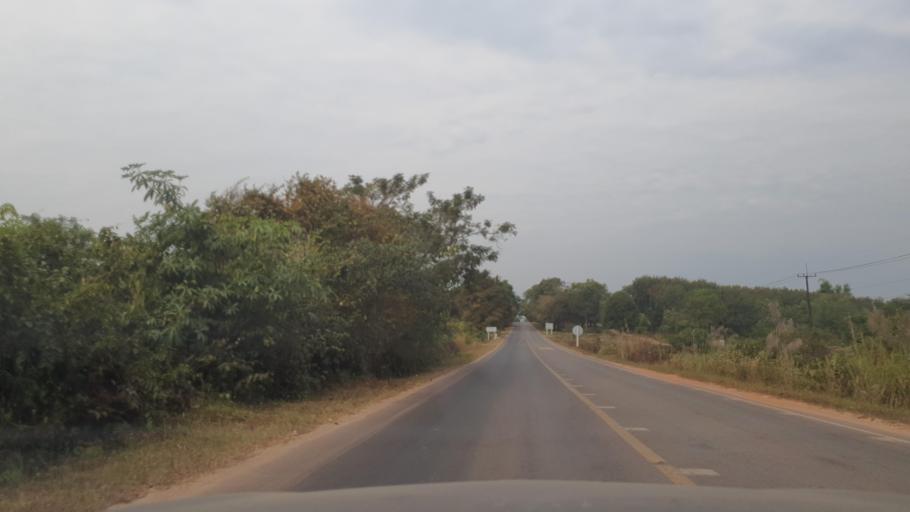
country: TH
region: Changwat Bueng Kan
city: Bung Khla
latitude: 18.2409
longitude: 104.0224
